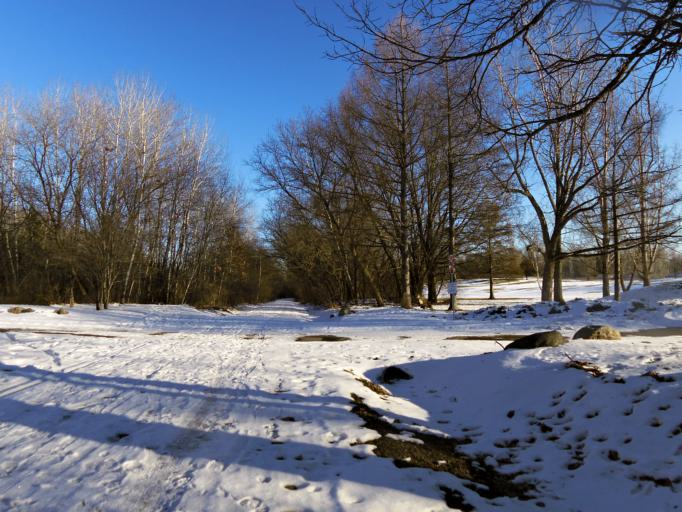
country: US
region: Minnesota
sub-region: Washington County
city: Grant
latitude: 45.0783
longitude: -92.8804
